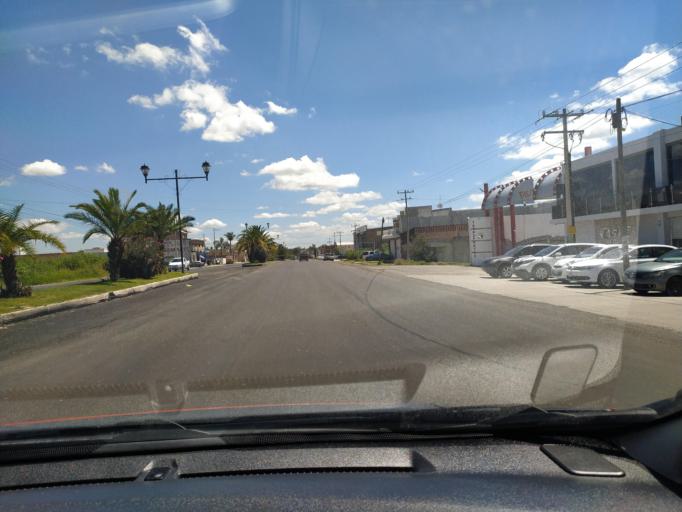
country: MX
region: Jalisco
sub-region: San Julian
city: Colonia Veintitres de Mayo
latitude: 21.0126
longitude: -102.1961
